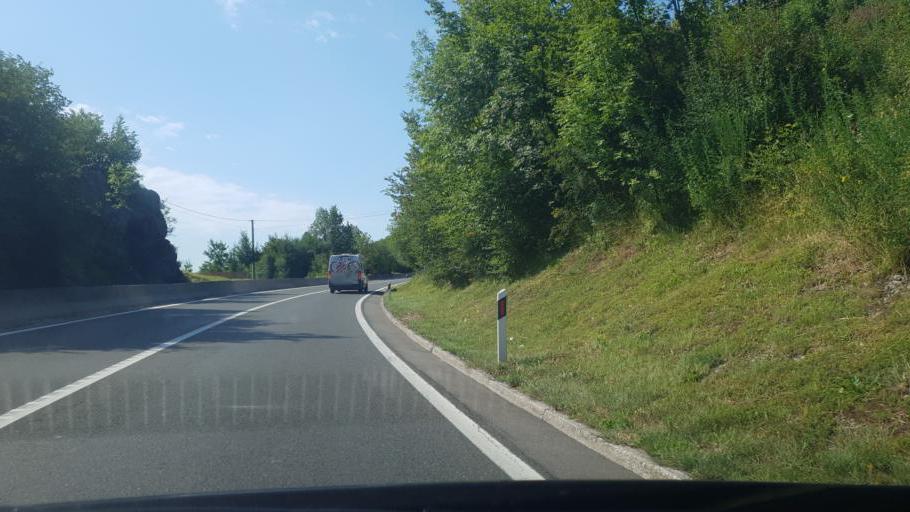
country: HR
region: Primorsko-Goranska
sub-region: Grad Opatija
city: Opatija
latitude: 45.3539
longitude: 14.3070
